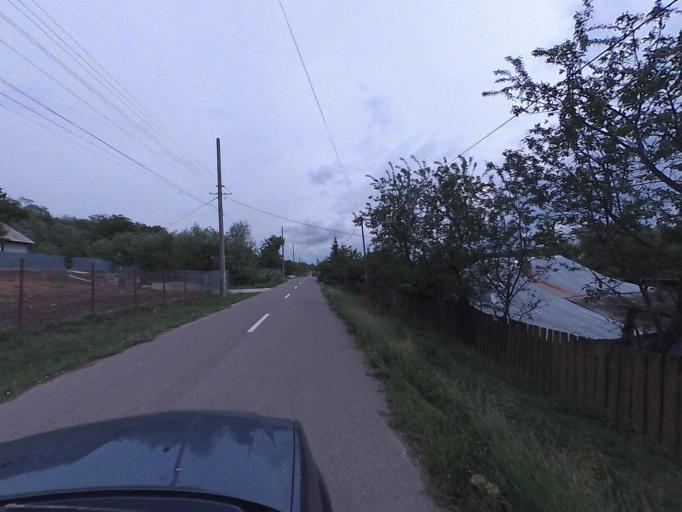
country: RO
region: Neamt
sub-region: Comuna Dulcesti
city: Dulcesti
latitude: 46.9596
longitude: 26.7944
